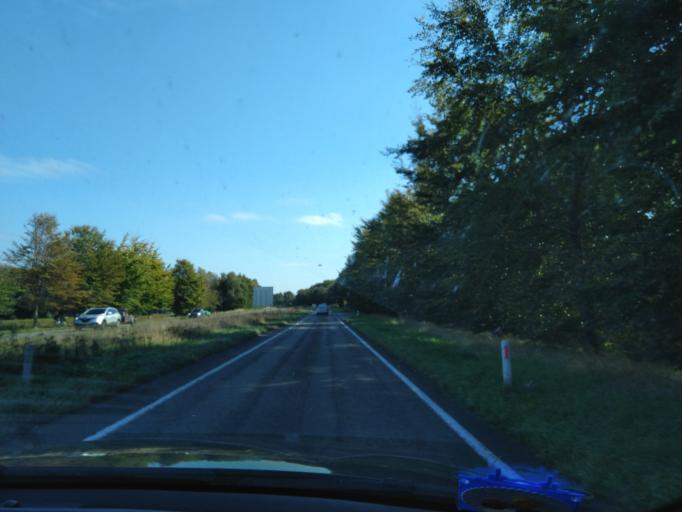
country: NL
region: Groningen
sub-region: Gemeente Veendam
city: Veendam
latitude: 53.0961
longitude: 6.9017
